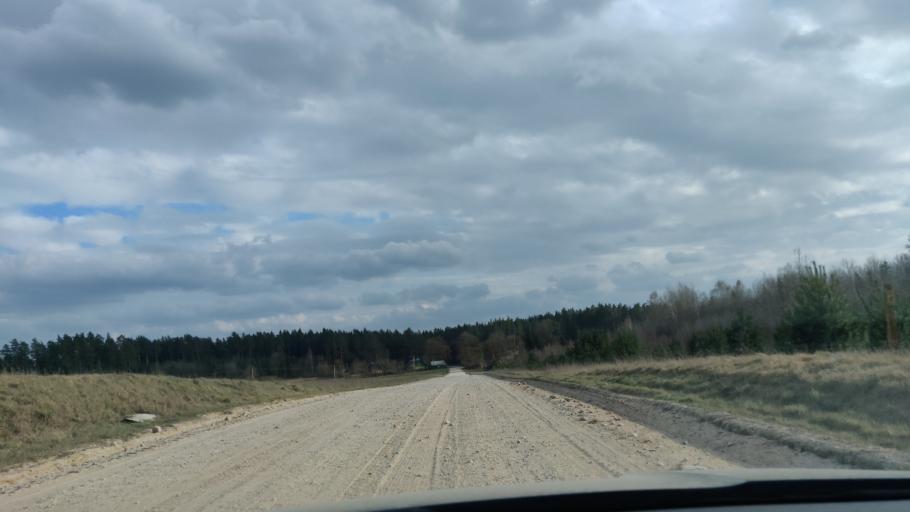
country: LT
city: Lentvaris
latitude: 54.6061
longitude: 25.0746
